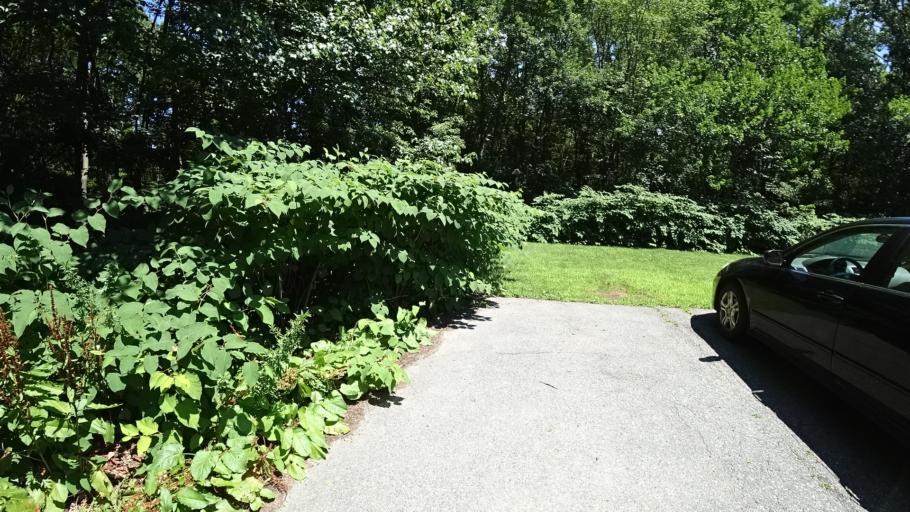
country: US
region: Massachusetts
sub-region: Norfolk County
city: Dedham
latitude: 42.2167
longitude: -71.1527
